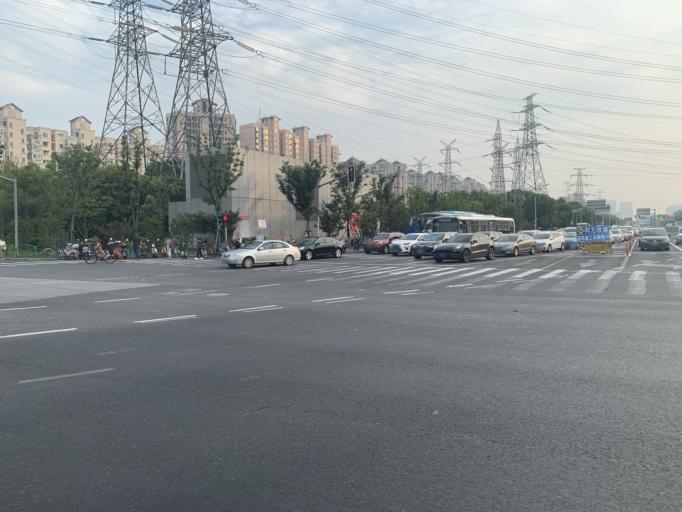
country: CN
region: Shanghai Shi
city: Huamu
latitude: 31.2432
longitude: 121.5736
